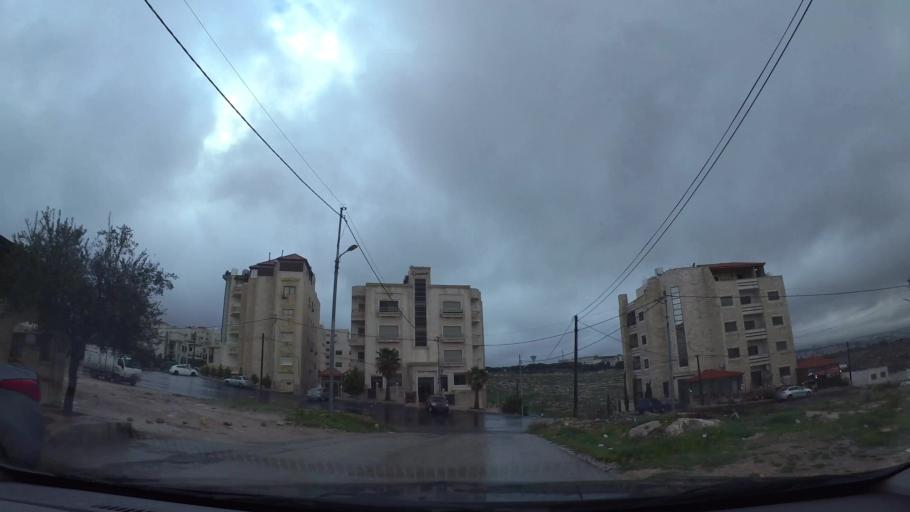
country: JO
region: Amman
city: Amman
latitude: 32.0036
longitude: 35.9275
